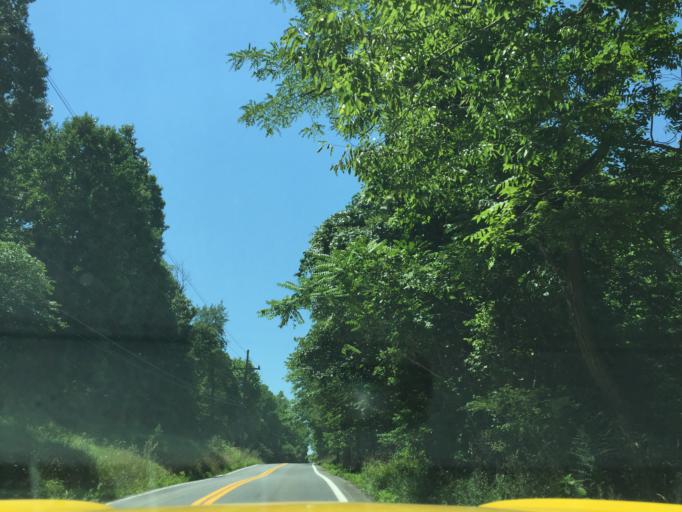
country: US
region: West Virginia
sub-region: Jefferson County
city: Bolivar
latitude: 39.3328
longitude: -77.7621
